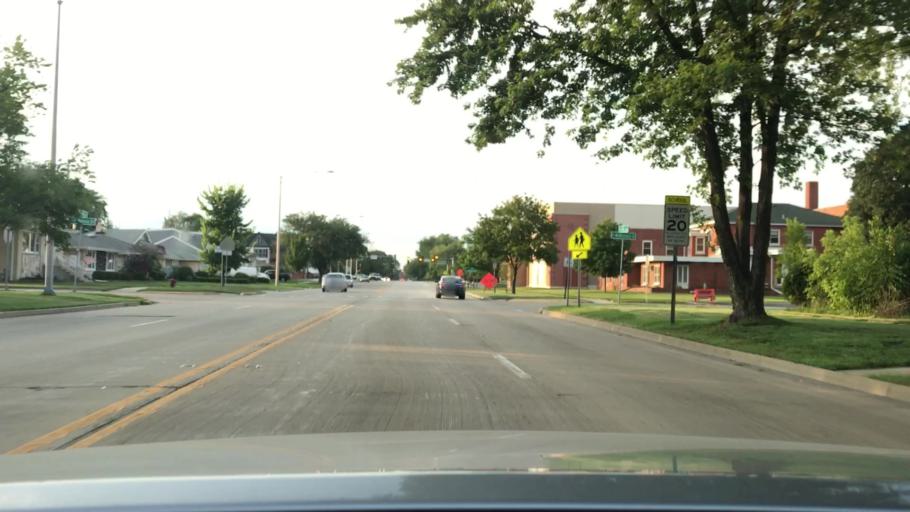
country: US
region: Illinois
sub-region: Cook County
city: Oak Lawn
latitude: 41.7212
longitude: -87.7603
